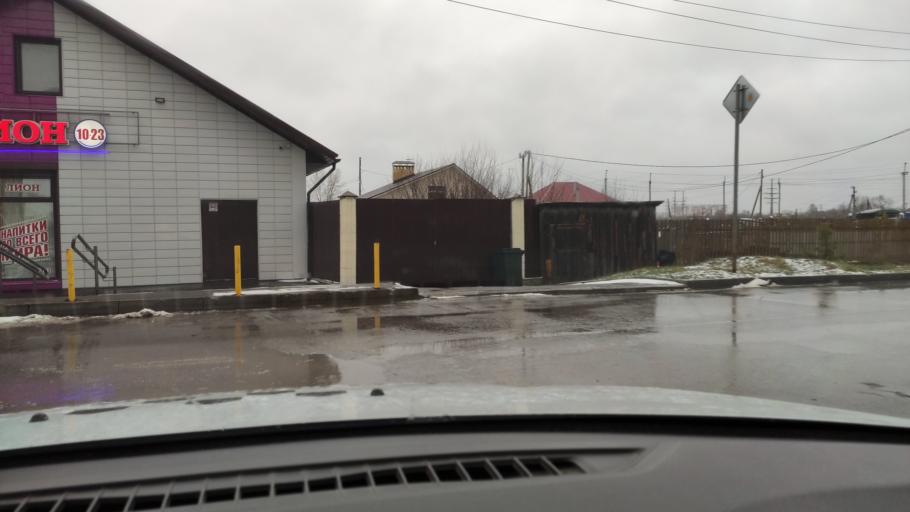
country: RU
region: Perm
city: Kondratovo
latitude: 57.9888
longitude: 56.1161
